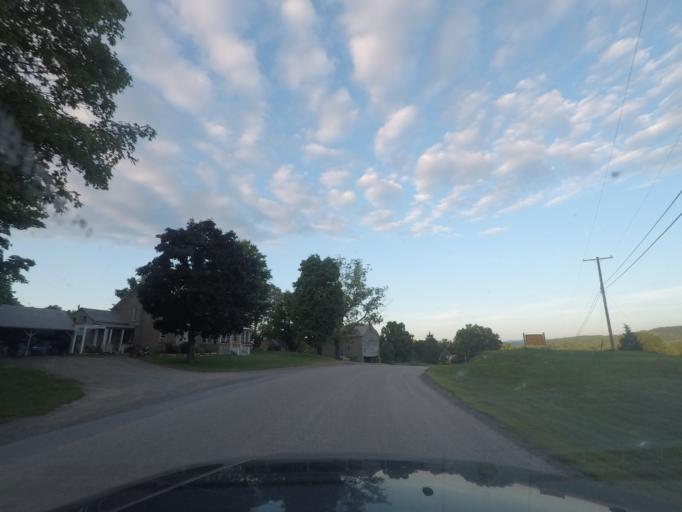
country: US
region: New York
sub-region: Rensselaer County
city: Nassau
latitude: 42.4910
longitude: -73.5727
